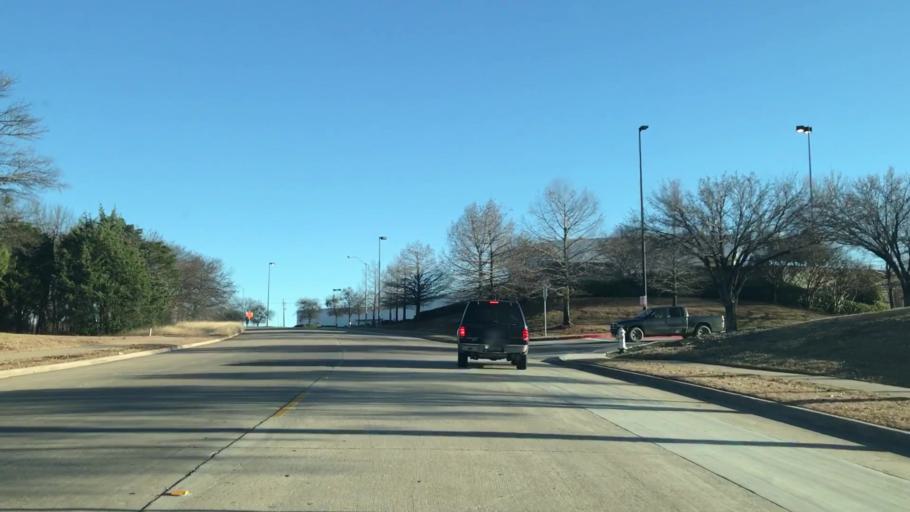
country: US
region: Texas
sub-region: Rockwall County
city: Rockwall
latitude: 32.9024
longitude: -96.4603
